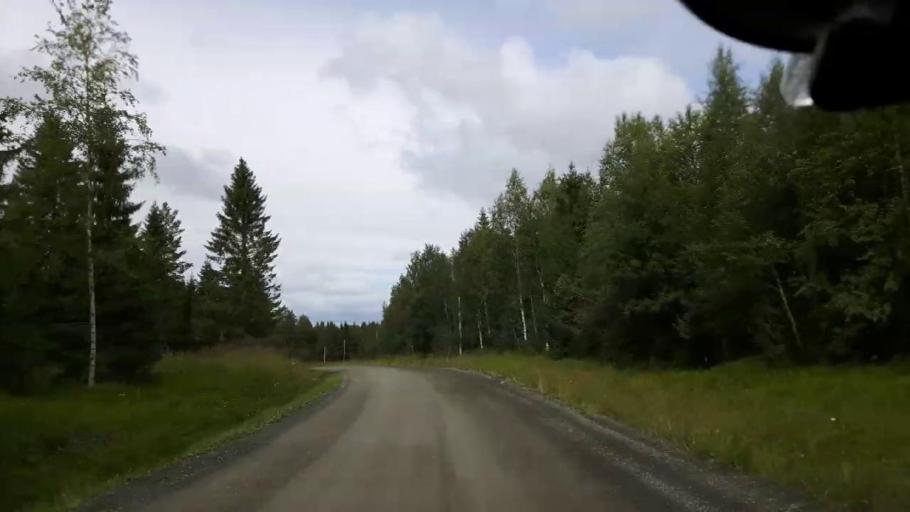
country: SE
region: Jaemtland
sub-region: Krokoms Kommun
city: Krokom
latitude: 63.3883
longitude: 14.1119
